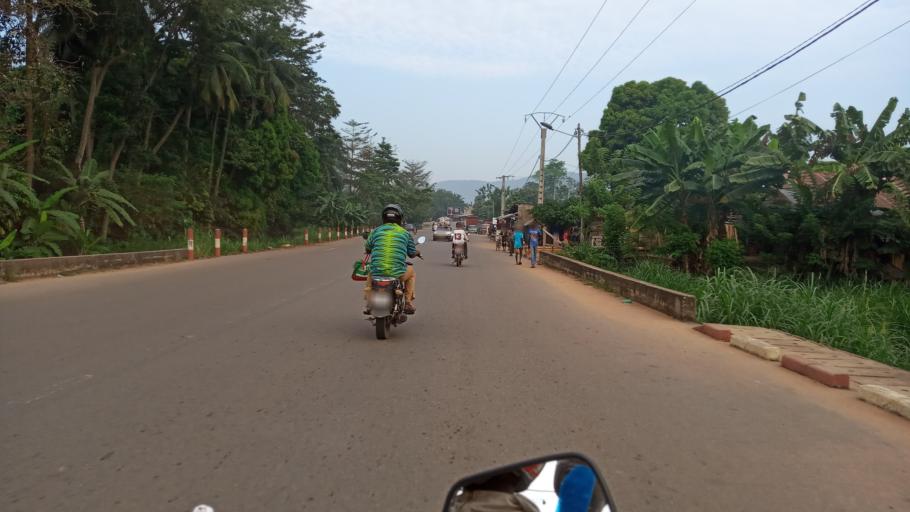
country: TG
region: Plateaux
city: Kpalime
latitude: 6.9026
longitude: 0.6332
